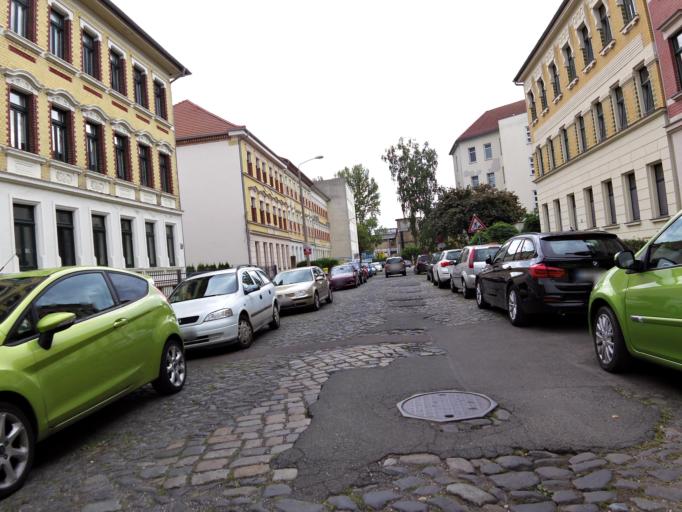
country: DE
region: Saxony
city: Leipzig
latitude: 51.3641
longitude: 12.4050
